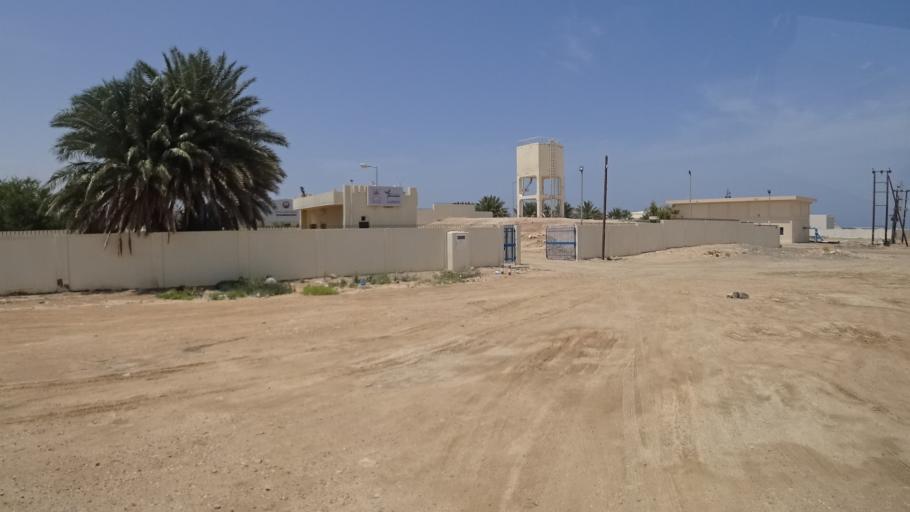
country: OM
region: Ash Sharqiyah
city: Sur
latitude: 22.6202
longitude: 59.4556
